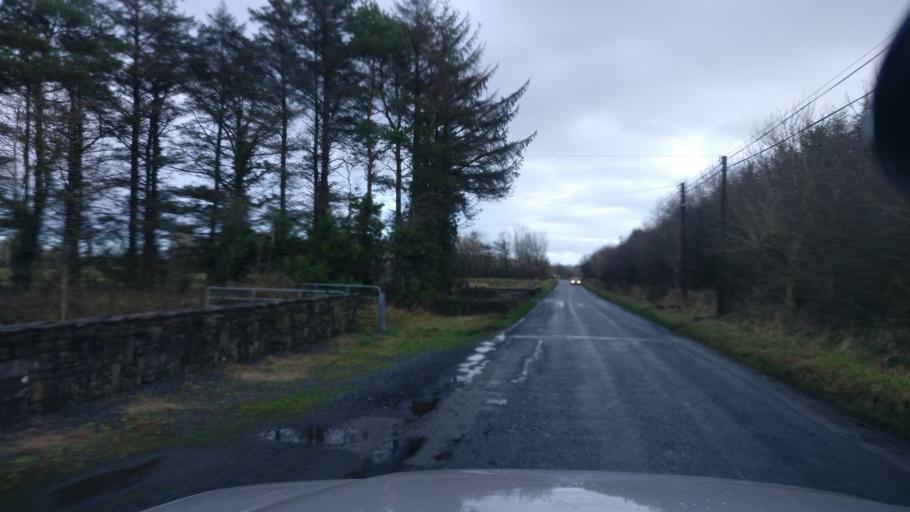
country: IE
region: Connaught
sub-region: County Galway
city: Athenry
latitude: 53.2972
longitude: -8.7033
